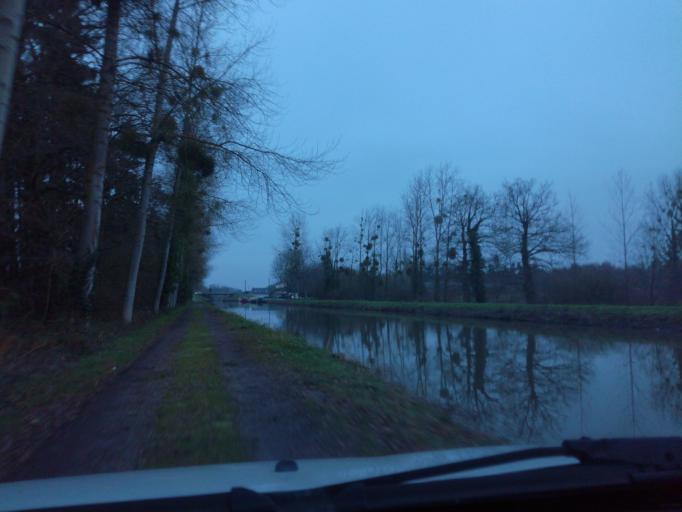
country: FR
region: Brittany
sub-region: Departement d'Ille-et-Vilaine
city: Chavagne
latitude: 48.0622
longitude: -1.7623
